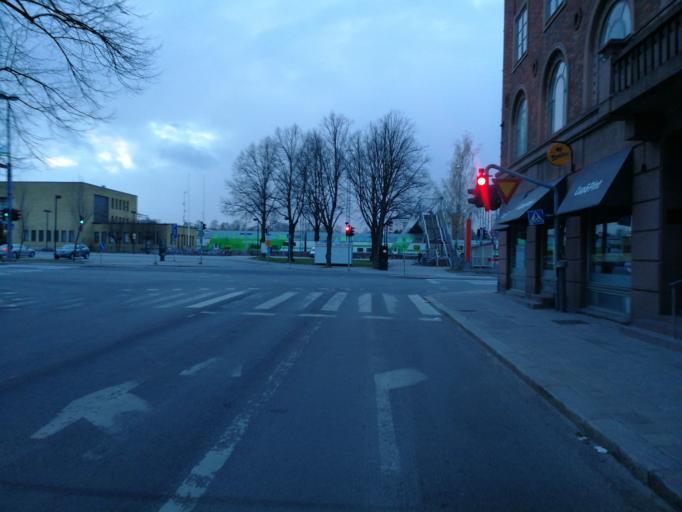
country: FI
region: Varsinais-Suomi
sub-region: Turku
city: Turku
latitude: 60.4536
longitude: 22.2549
